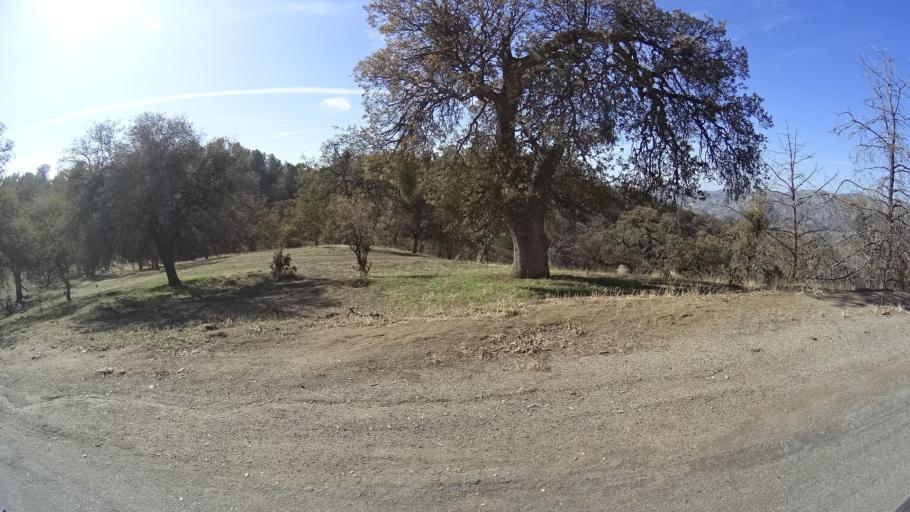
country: US
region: California
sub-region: Kern County
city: Bear Valley Springs
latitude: 35.3563
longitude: -118.5629
